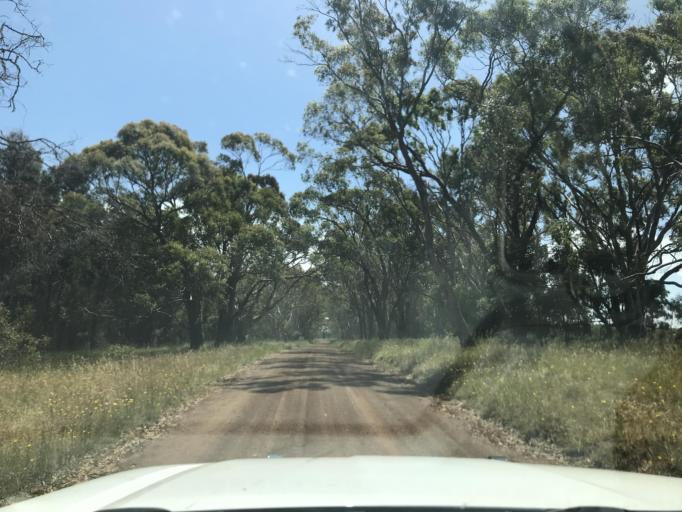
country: AU
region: South Australia
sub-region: Wattle Range
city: Penola
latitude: -37.2878
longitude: 141.4799
